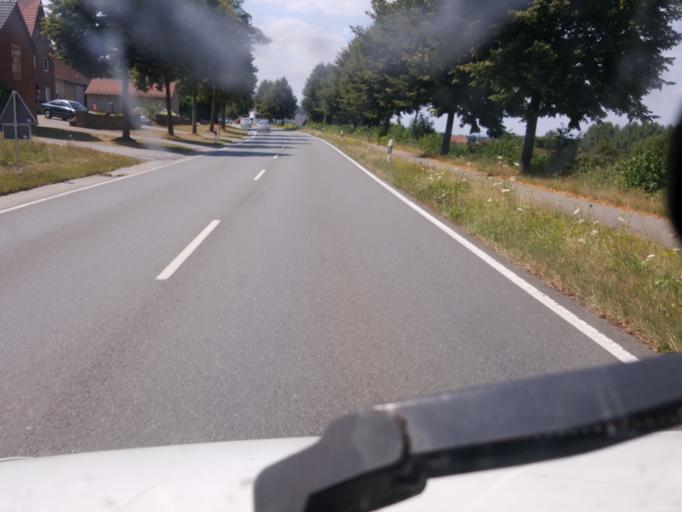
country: DE
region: North Rhine-Westphalia
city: Bad Oeynhausen
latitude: 52.2716
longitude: 8.7891
